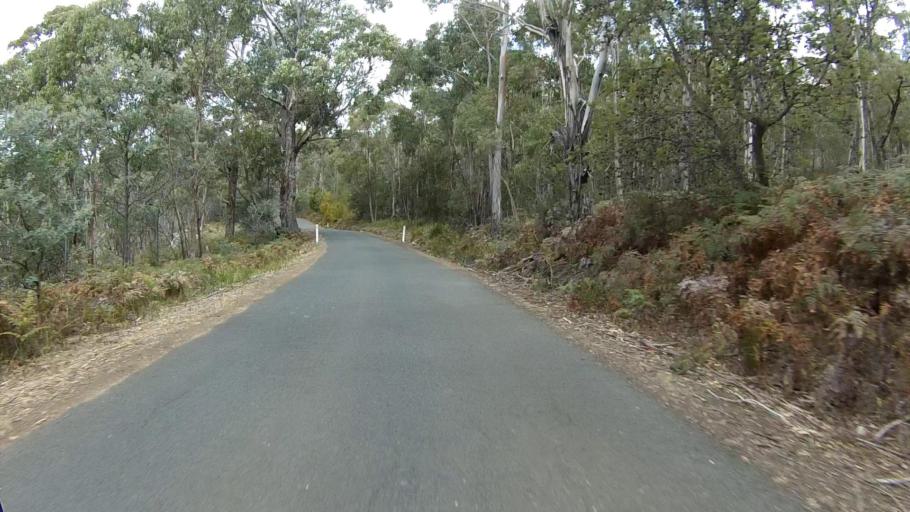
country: AU
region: Tasmania
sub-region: Sorell
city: Sorell
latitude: -42.6033
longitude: 147.9214
